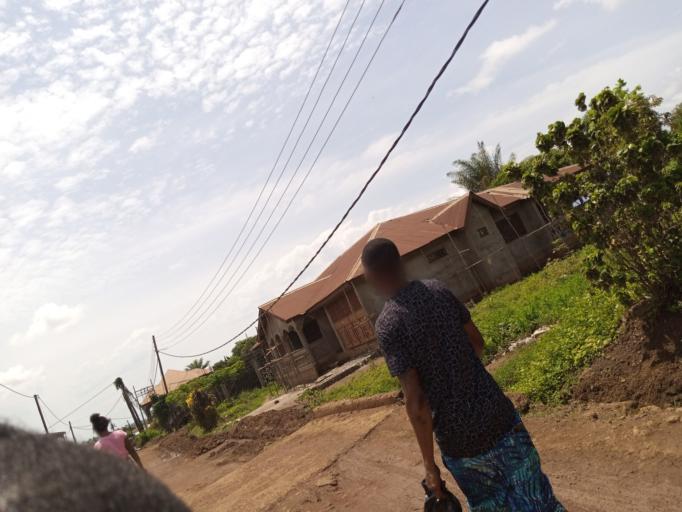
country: SL
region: Western Area
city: Hastings
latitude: 8.3798
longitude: -13.1352
